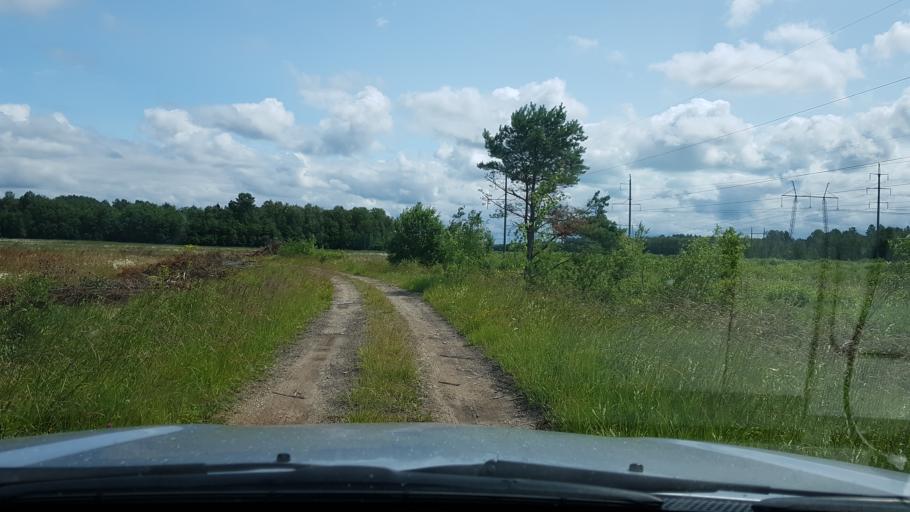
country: EE
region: Ida-Virumaa
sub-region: Sillamaee linn
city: Sillamae
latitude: 59.3603
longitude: 27.8097
